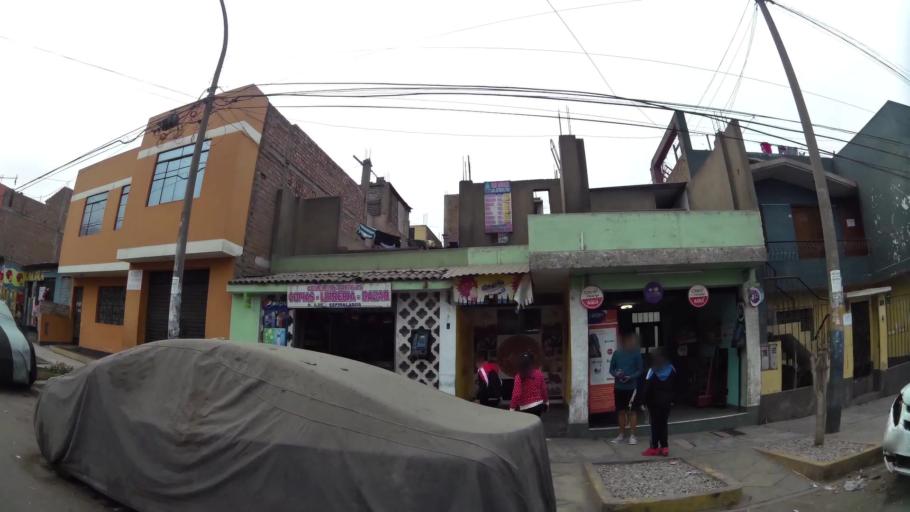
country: PE
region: Lima
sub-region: Lima
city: Independencia
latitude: -11.9837
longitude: -77.0149
